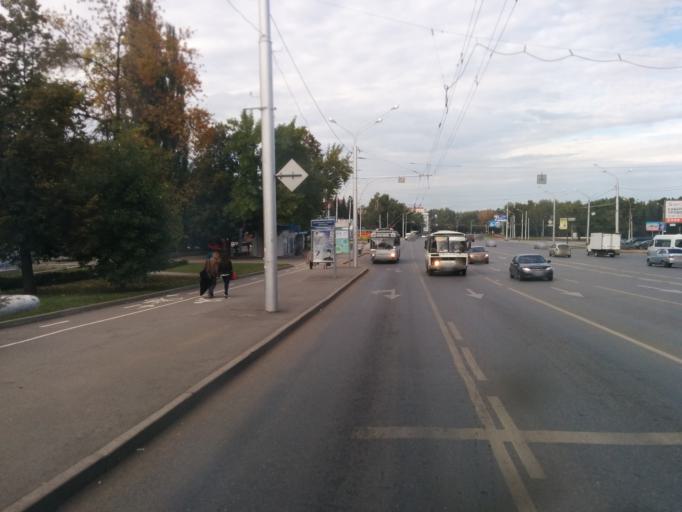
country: RU
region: Bashkortostan
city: Ufa
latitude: 54.7946
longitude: 56.0379
